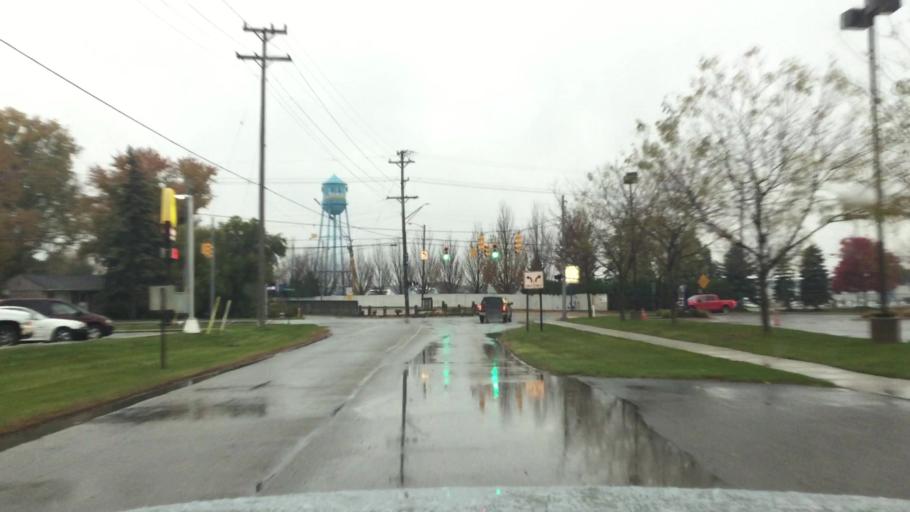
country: US
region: Michigan
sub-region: Saint Clair County
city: Algonac
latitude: 42.6152
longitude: -82.5422
